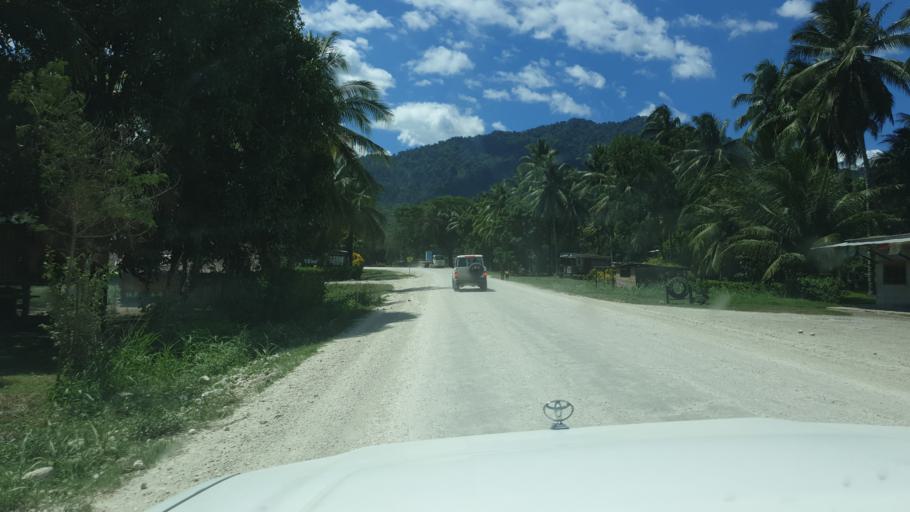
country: PG
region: Eastern Highlands
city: Goroka
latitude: -5.6364
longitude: 145.4863
